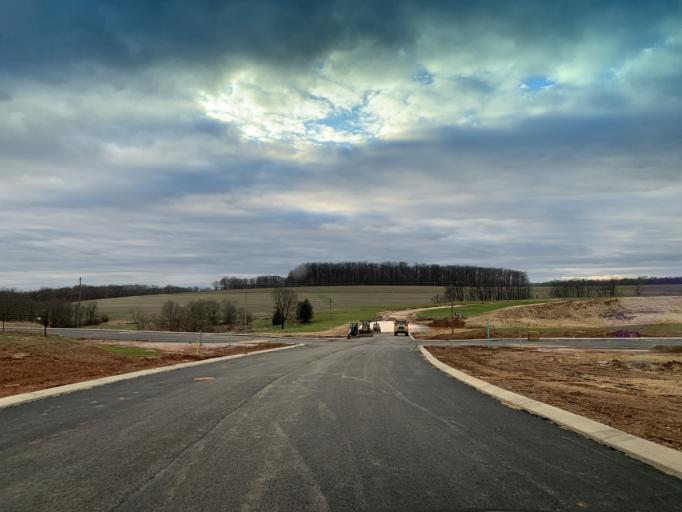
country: US
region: Pennsylvania
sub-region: York County
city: Stewartstown
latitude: 39.7697
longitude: -76.5931
